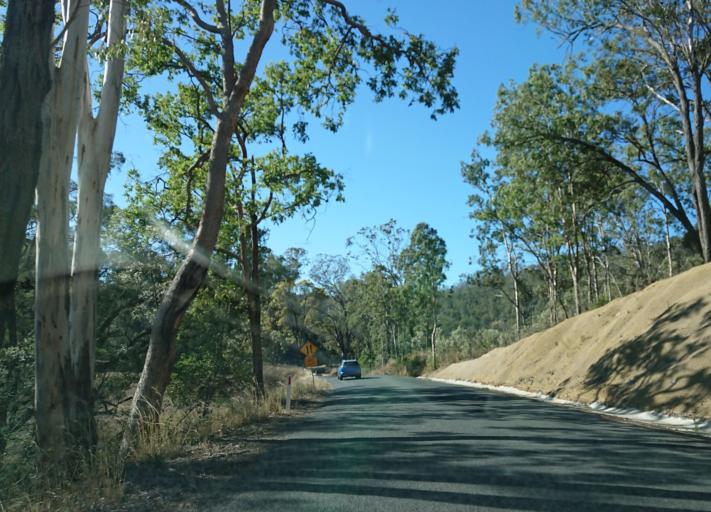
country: AU
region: Queensland
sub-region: Toowoomba
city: Top Camp
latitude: -27.7605
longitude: 152.0818
